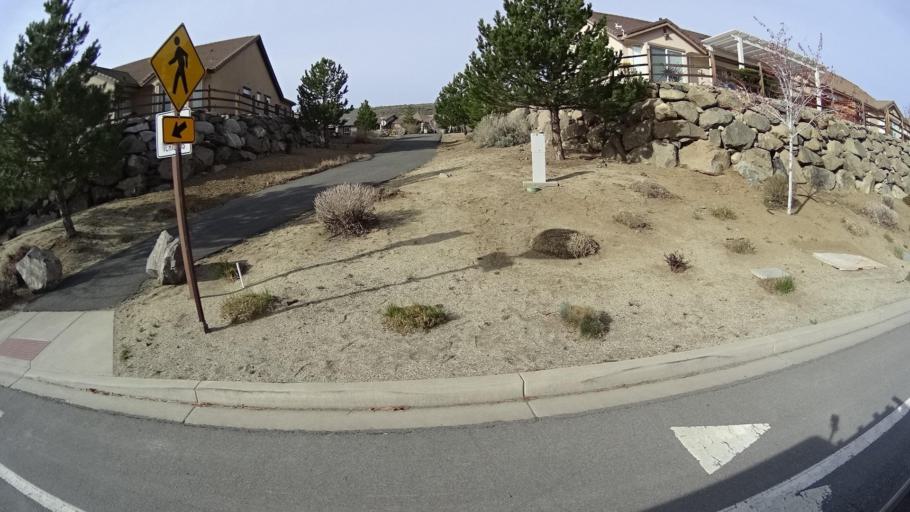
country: US
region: Nevada
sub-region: Washoe County
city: Mogul
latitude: 39.5204
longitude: -119.9476
